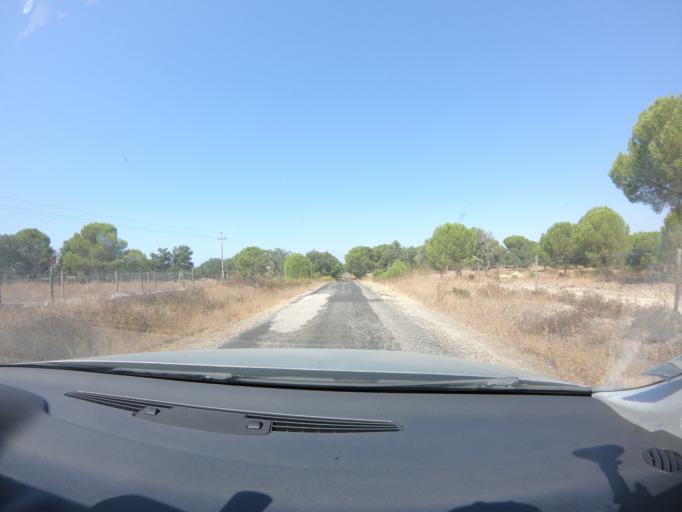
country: PT
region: Setubal
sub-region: Alcacer do Sal
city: Alcacer do Sal
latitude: 38.2625
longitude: -8.3109
